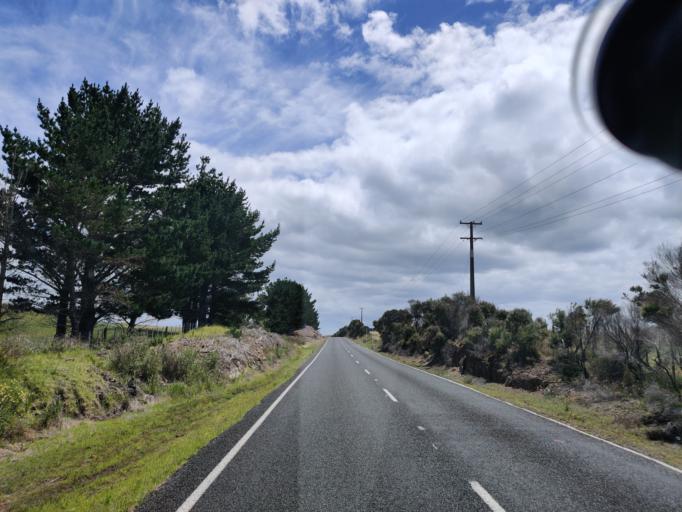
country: NZ
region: Northland
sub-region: Far North District
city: Kaitaia
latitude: -34.7216
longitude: 173.0418
